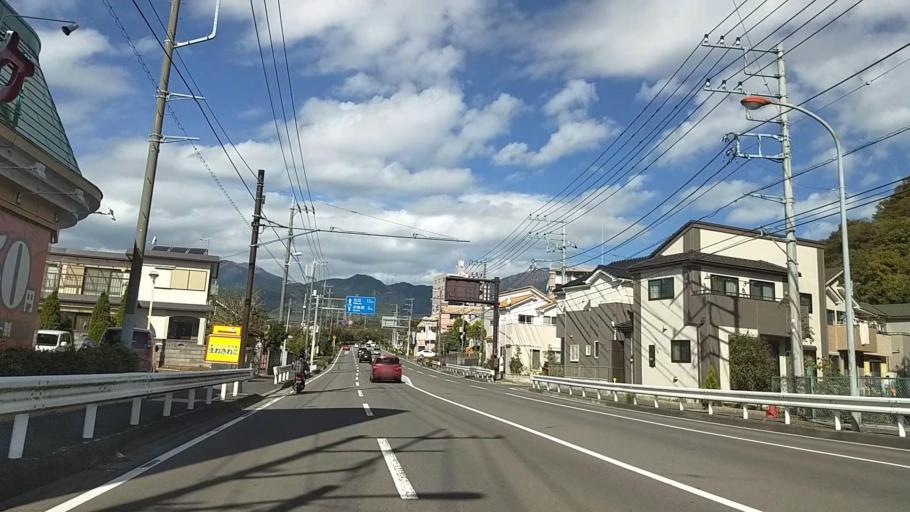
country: JP
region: Kanagawa
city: Hadano
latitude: 35.3709
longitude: 139.2360
